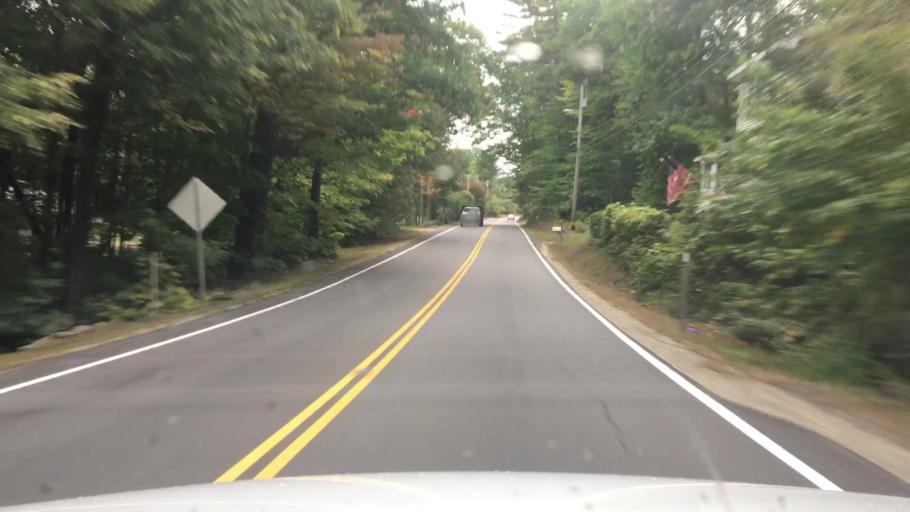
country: US
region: New Hampshire
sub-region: Belknap County
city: Gilford
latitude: 43.5510
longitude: -71.3106
